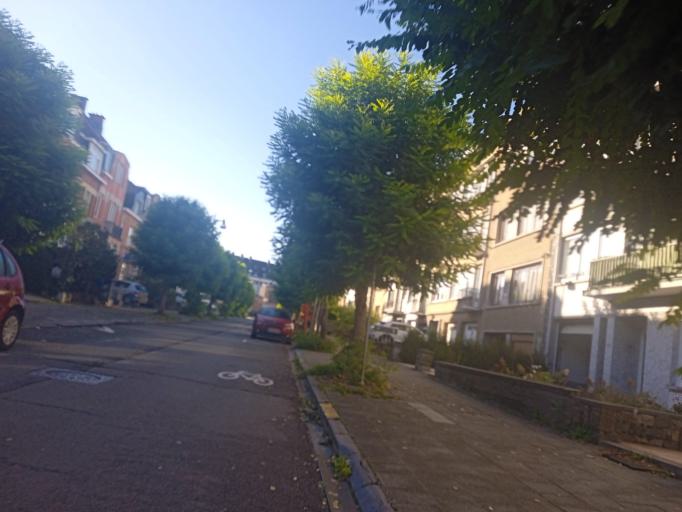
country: BE
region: Brussels Capital
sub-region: Bruxelles-Capitale
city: Brussels
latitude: 50.8486
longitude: 4.3075
